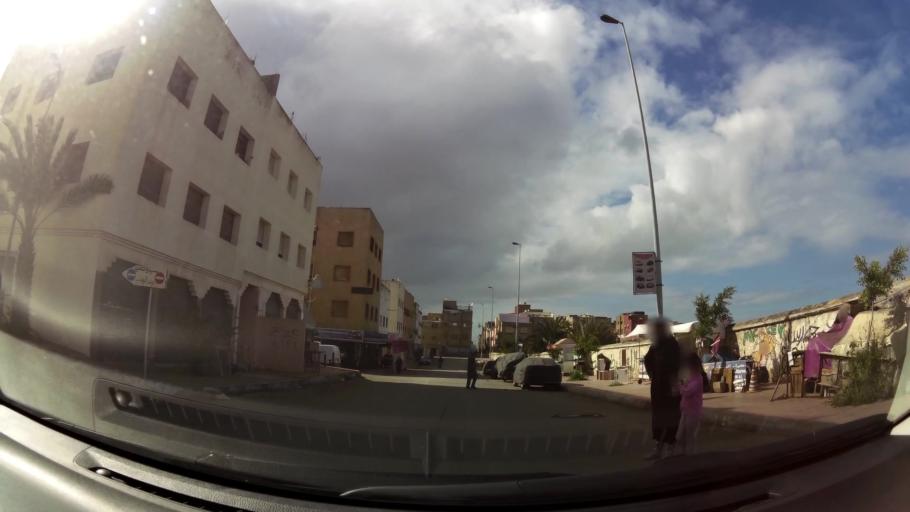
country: MA
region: Grand Casablanca
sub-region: Casablanca
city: Casablanca
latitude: 33.5589
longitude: -7.6964
